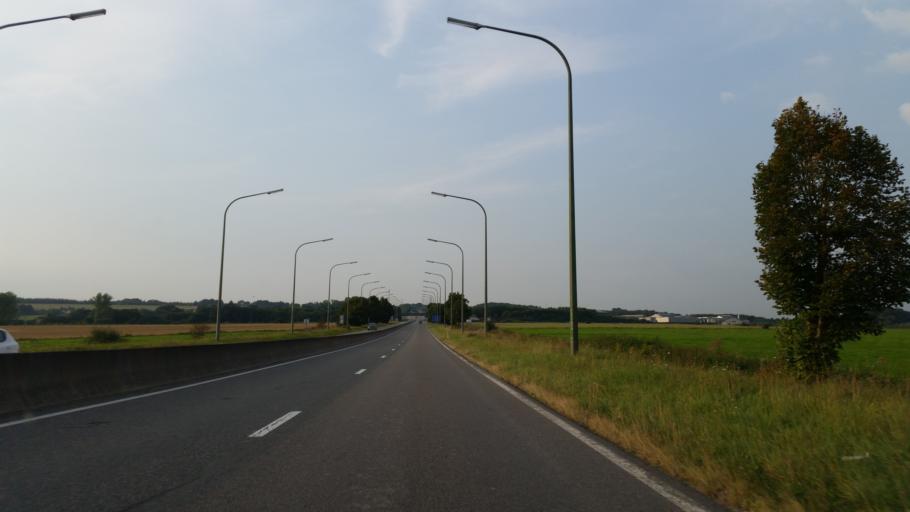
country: BE
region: Wallonia
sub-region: Province de Namur
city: Somme-Leuze
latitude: 50.2843
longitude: 5.3487
